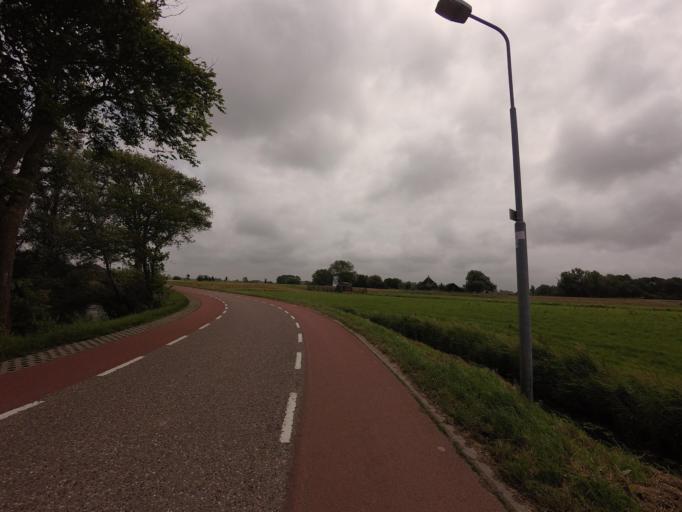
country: NL
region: North Holland
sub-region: Gemeente Schagen
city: Schagen
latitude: 52.7807
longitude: 4.7735
